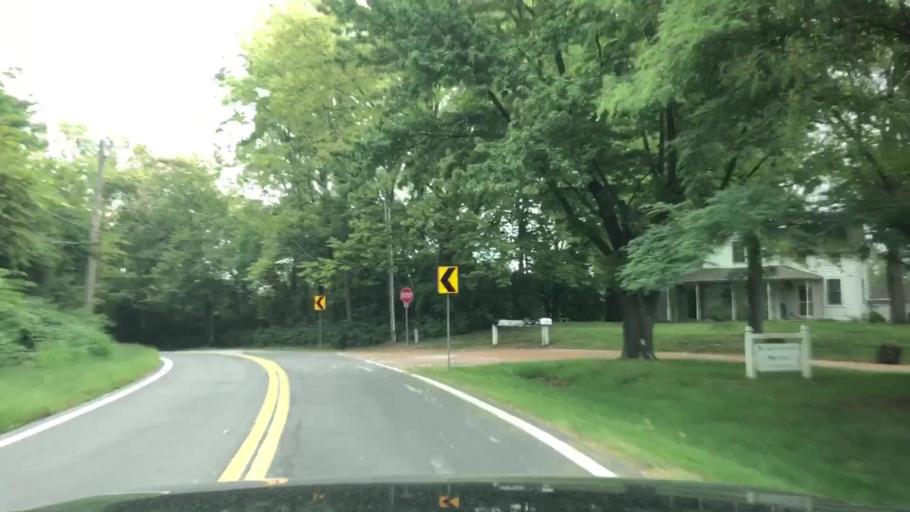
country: US
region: Missouri
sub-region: Saint Louis County
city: Hazelwood
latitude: 38.8141
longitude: -90.3718
